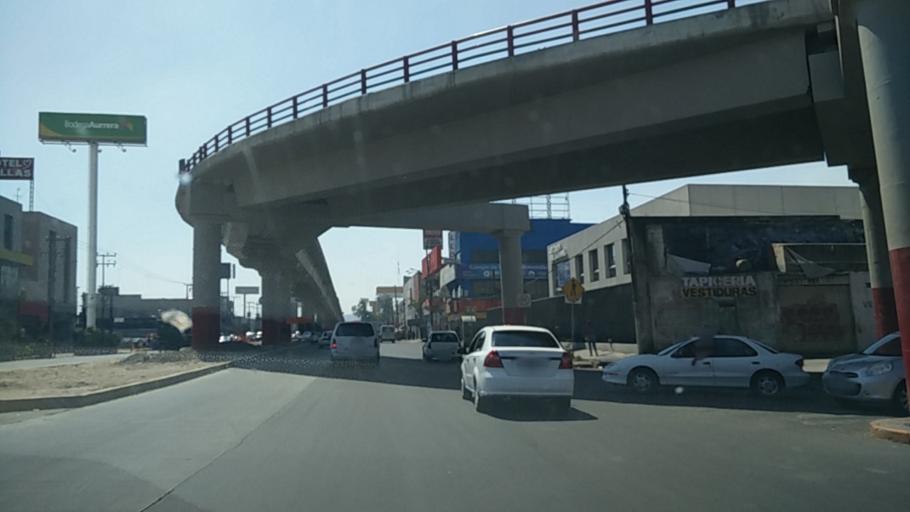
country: MX
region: Mexico
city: Ecatepec
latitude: 19.5990
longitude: -99.0361
